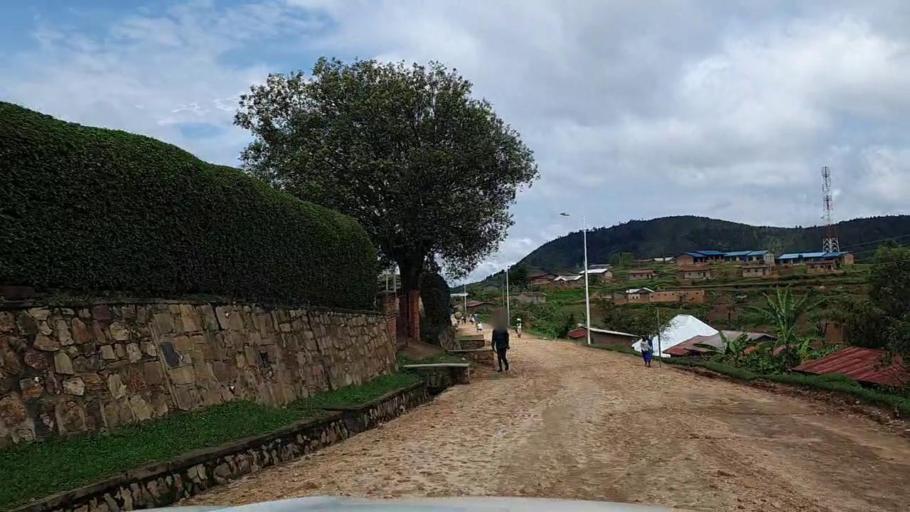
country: RW
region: Southern Province
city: Gikongoro
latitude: -2.3319
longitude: 29.5279
